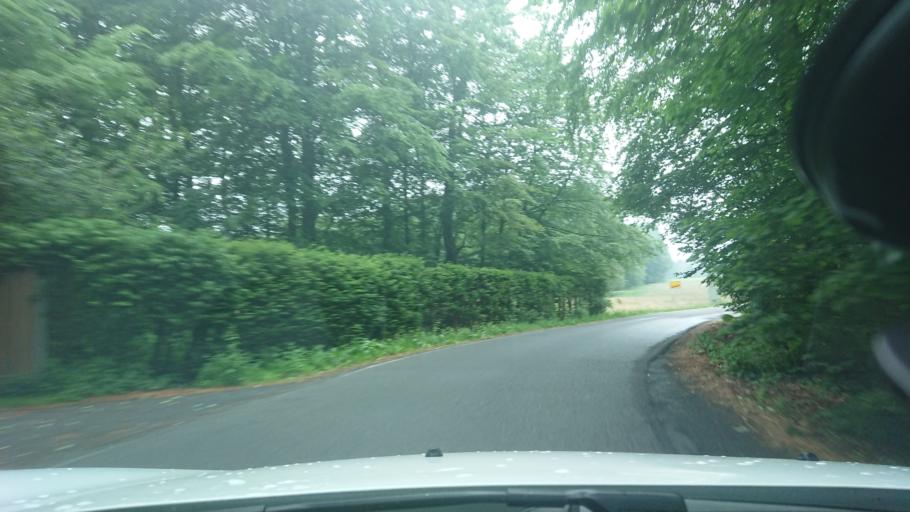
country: DE
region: North Rhine-Westphalia
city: Wermelskirchen
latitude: 51.1406
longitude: 7.2570
